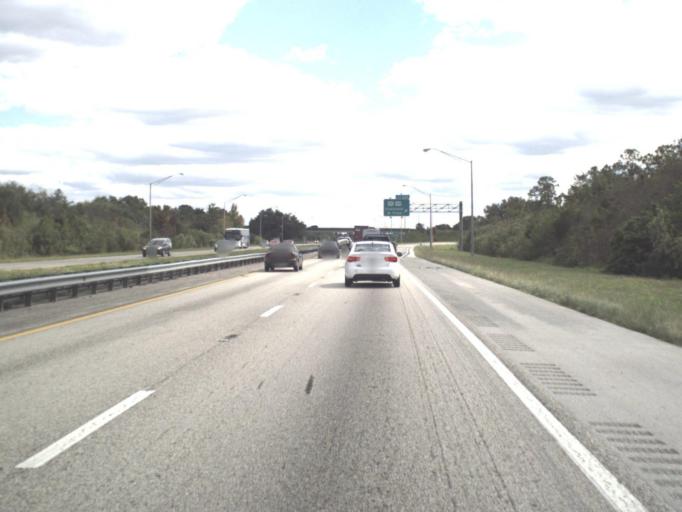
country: US
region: Florida
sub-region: Osceola County
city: Buenaventura Lakes
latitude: 28.2917
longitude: -81.3508
